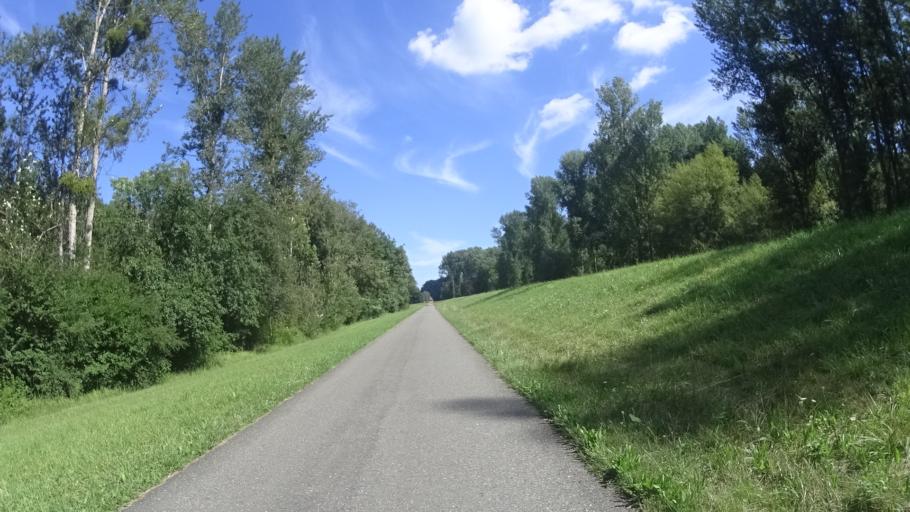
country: DE
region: Rheinland-Pfalz
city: Hordt
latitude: 49.1731
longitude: 8.3667
